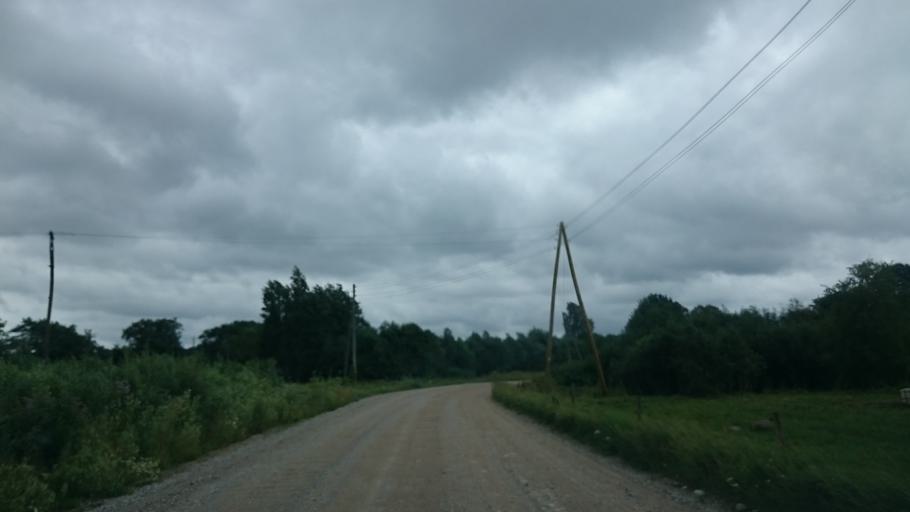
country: LV
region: Durbe
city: Liegi
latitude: 56.7509
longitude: 21.3623
